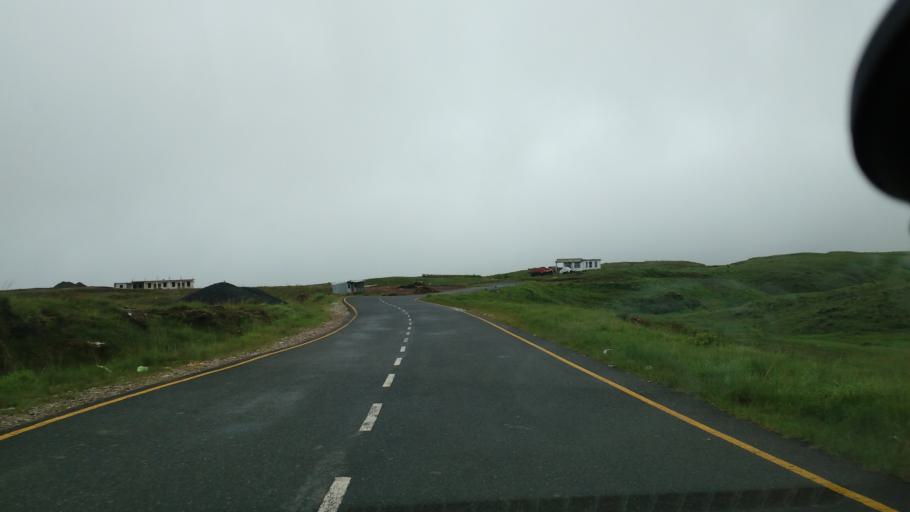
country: IN
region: Meghalaya
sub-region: East Khasi Hills
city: Cherrapunji
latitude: 25.3215
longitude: 91.7351
